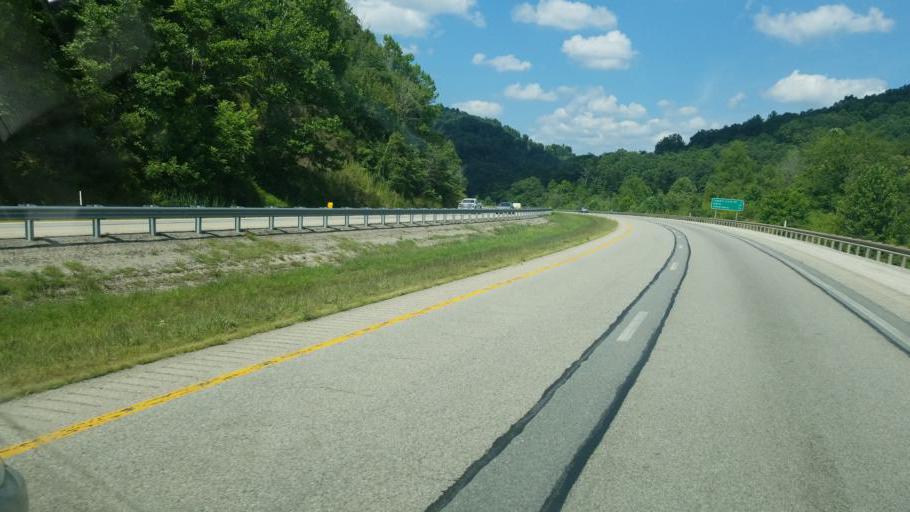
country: US
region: West Virginia
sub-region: Kanawha County
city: Charleston
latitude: 38.4224
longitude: -81.6244
